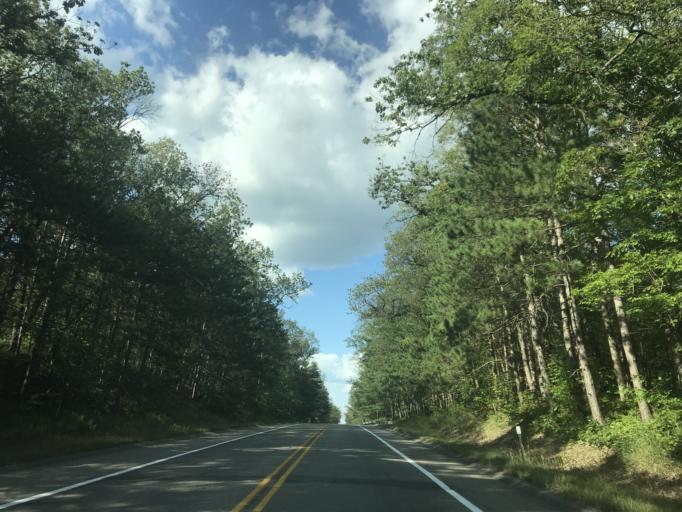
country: US
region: Michigan
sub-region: Newaygo County
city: Newaygo
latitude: 43.4591
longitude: -85.7785
